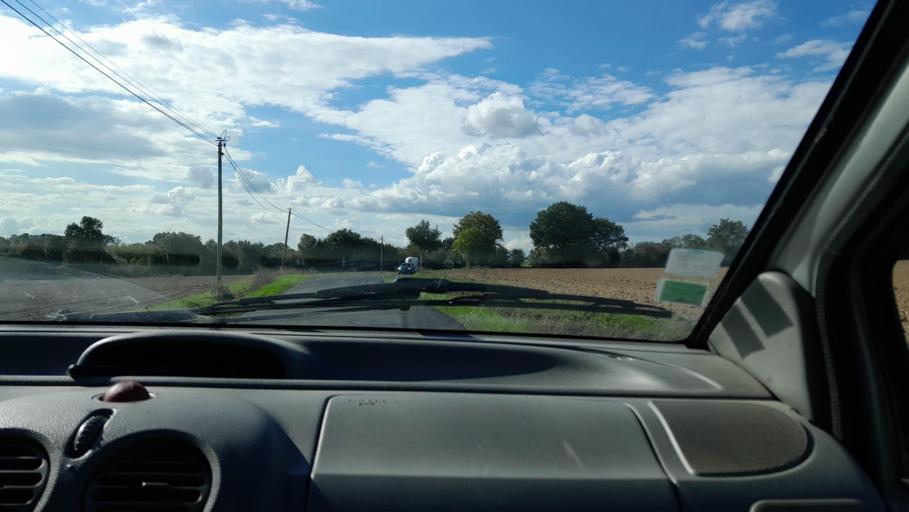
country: FR
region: Pays de la Loire
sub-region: Departement de la Mayenne
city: Ahuille
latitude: 48.0217
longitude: -0.8802
